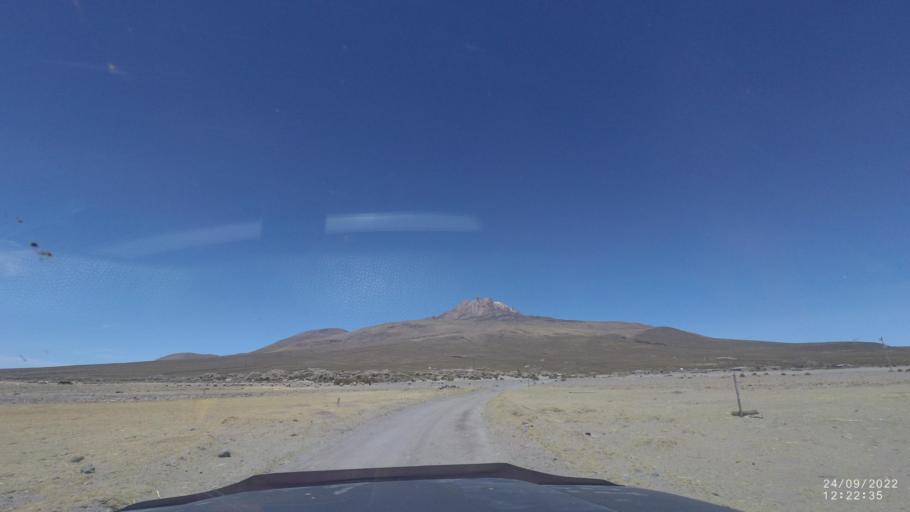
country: BO
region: Potosi
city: Colchani
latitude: -19.7575
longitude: -67.6646
